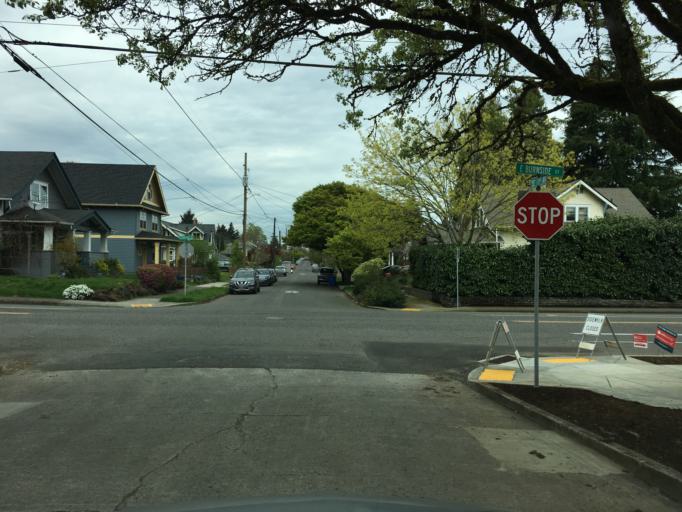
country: US
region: Oregon
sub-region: Multnomah County
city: Lents
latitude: 45.5229
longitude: -122.5899
